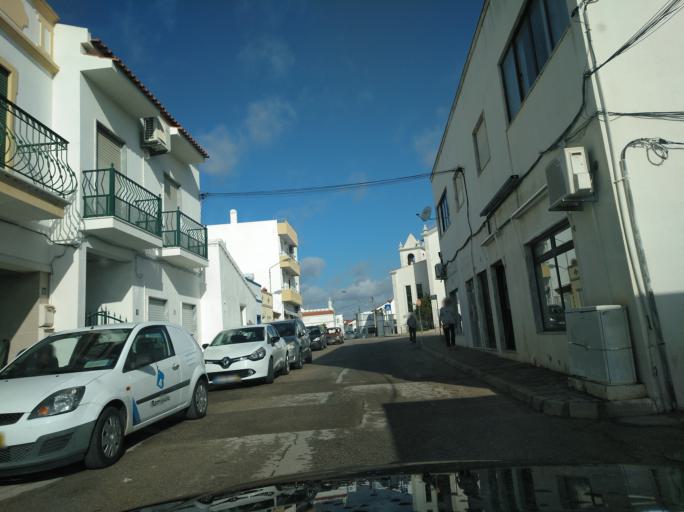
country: PT
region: Faro
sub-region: Vila Real de Santo Antonio
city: Monte Gordo
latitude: 37.1772
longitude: -7.5004
